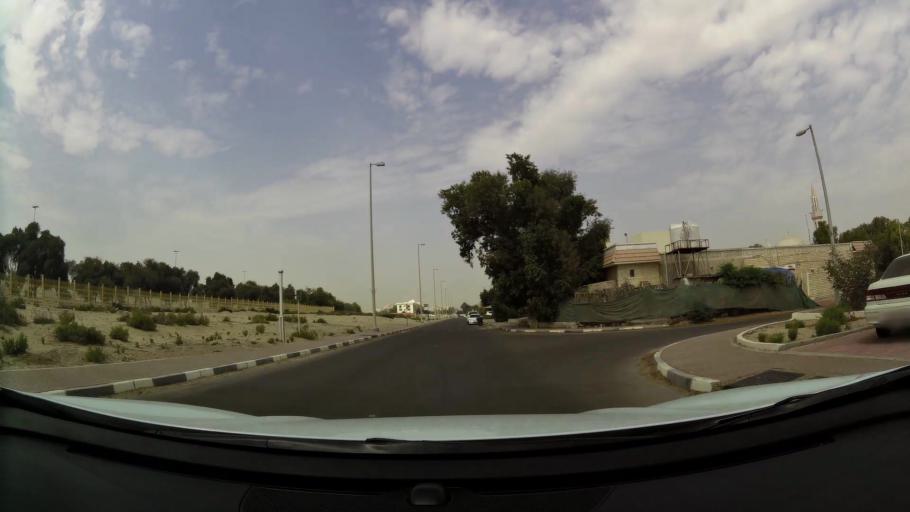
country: AE
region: Abu Dhabi
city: Abu Dhabi
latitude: 24.3019
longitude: 54.6216
